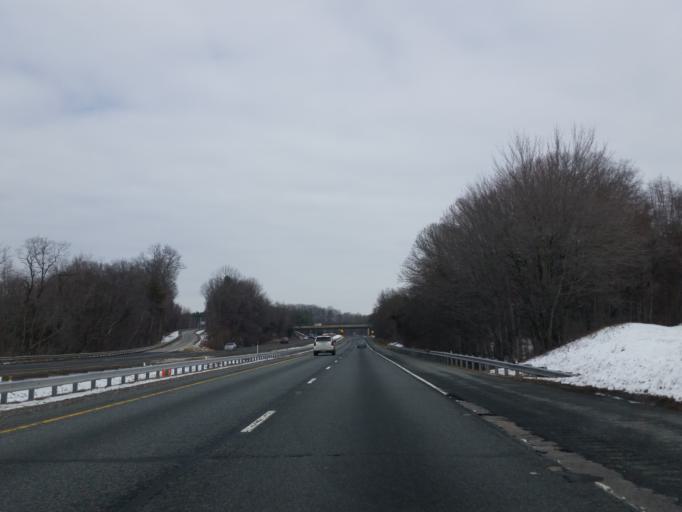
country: US
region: Maryland
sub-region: Baltimore County
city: Hunt Valley
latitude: 39.5878
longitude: -76.6753
